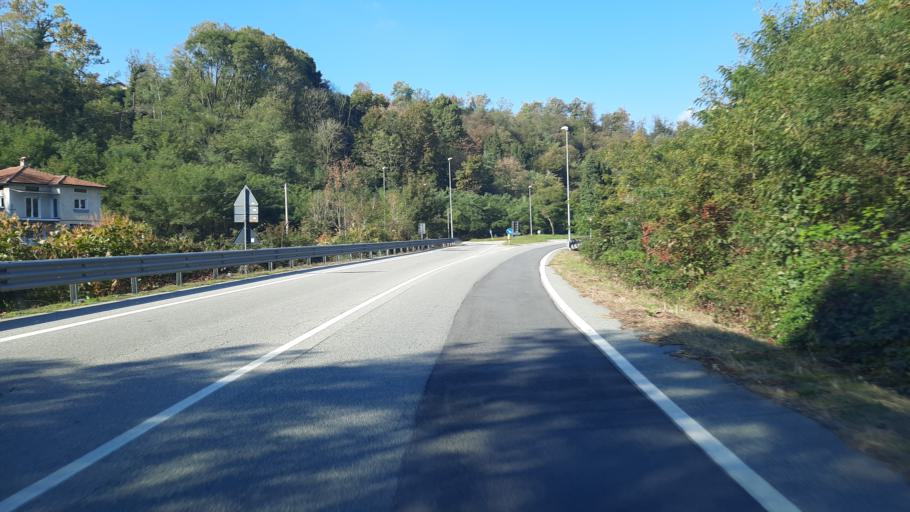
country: IT
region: Piedmont
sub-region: Provincia di Novara
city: Gozzano
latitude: 45.7423
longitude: 8.4243
